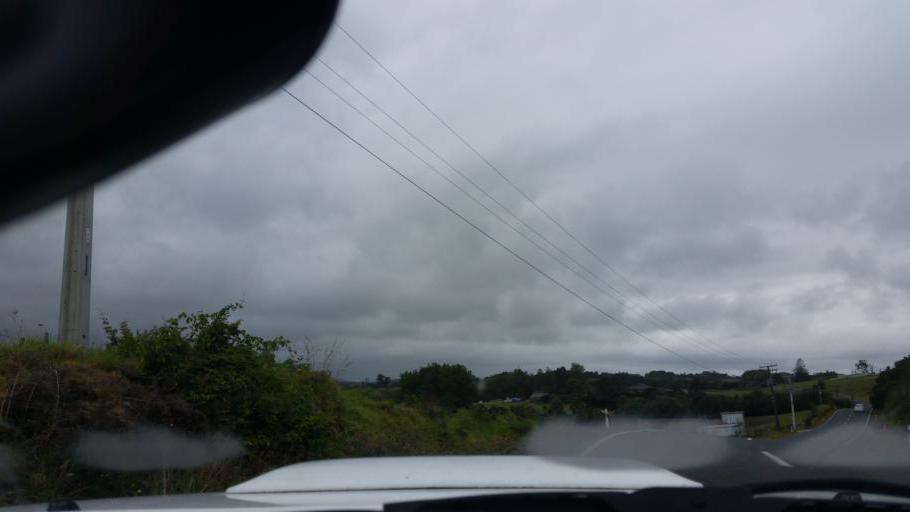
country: NZ
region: Auckland
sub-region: Auckland
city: Wellsford
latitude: -36.1591
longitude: 174.4544
